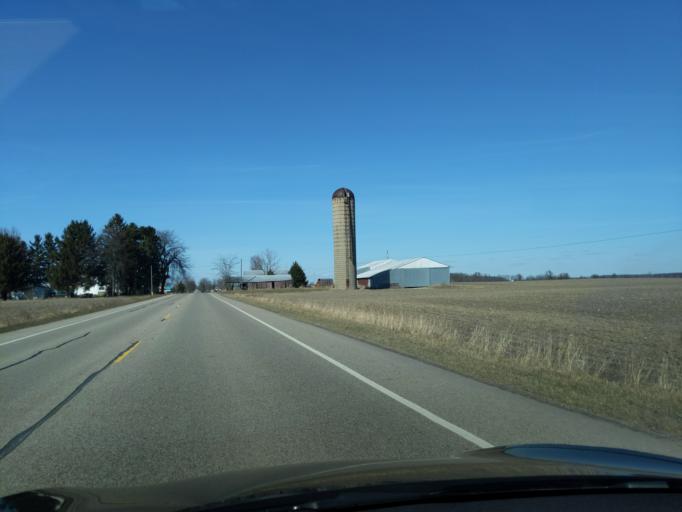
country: US
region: Michigan
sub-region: Ionia County
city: Lake Odessa
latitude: 42.8251
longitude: -85.1337
